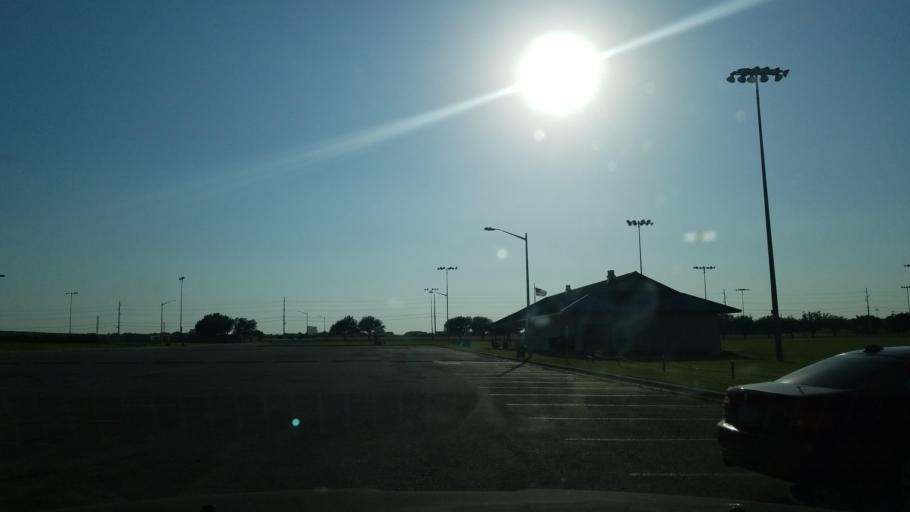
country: US
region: Texas
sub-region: Denton County
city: Denton
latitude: 33.2426
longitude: -97.1556
